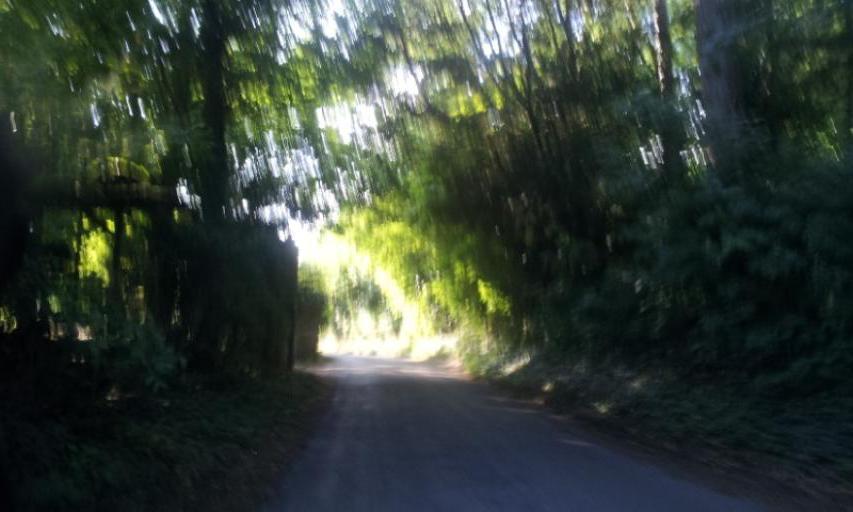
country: GB
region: England
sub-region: Kent
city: Boxley
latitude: 51.2909
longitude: 0.5907
